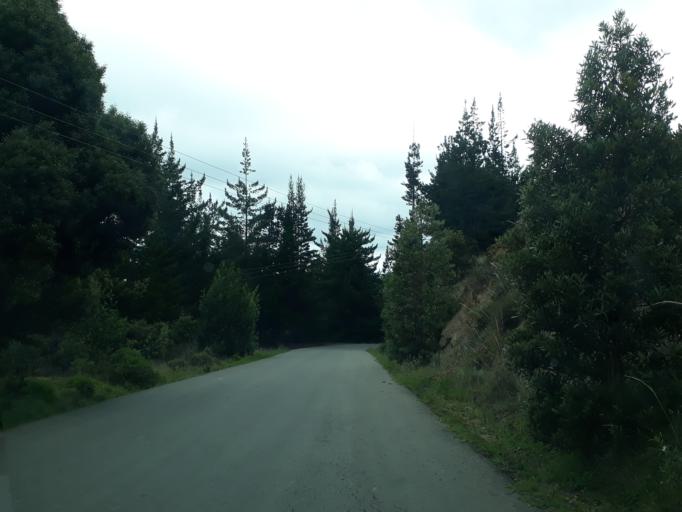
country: CO
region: Cundinamarca
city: Cucunuba
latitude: 5.2132
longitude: -73.7840
